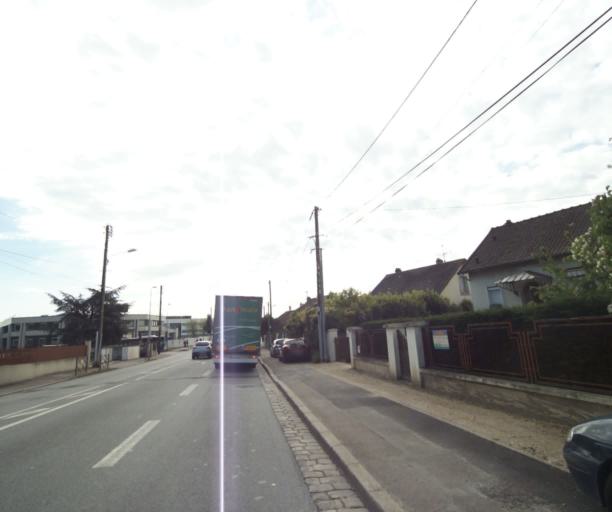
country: FR
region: Ile-de-France
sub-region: Departement des Yvelines
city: Les Mureaux
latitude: 48.9986
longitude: 1.9217
